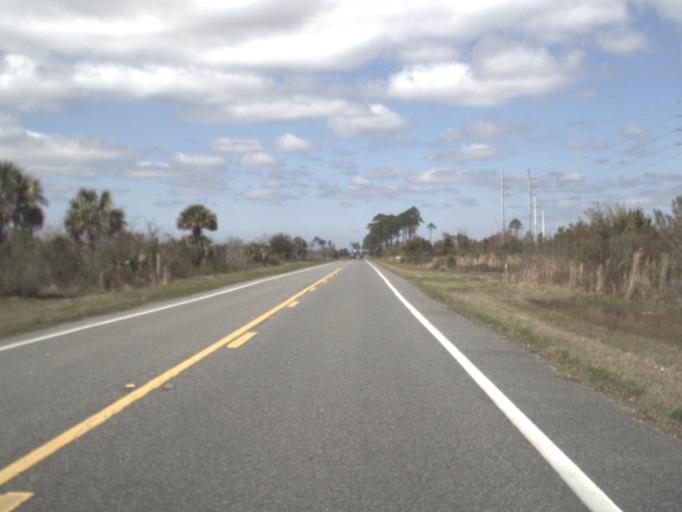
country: US
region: Florida
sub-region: Franklin County
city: Apalachicola
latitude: 29.7197
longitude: -85.0658
